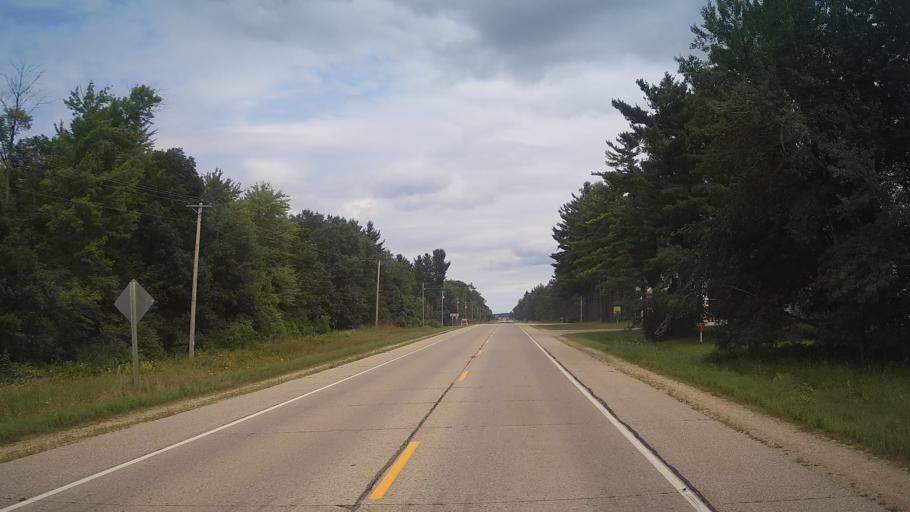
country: US
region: Wisconsin
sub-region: Waushara County
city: Redgranite
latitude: 44.0375
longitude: -89.0839
